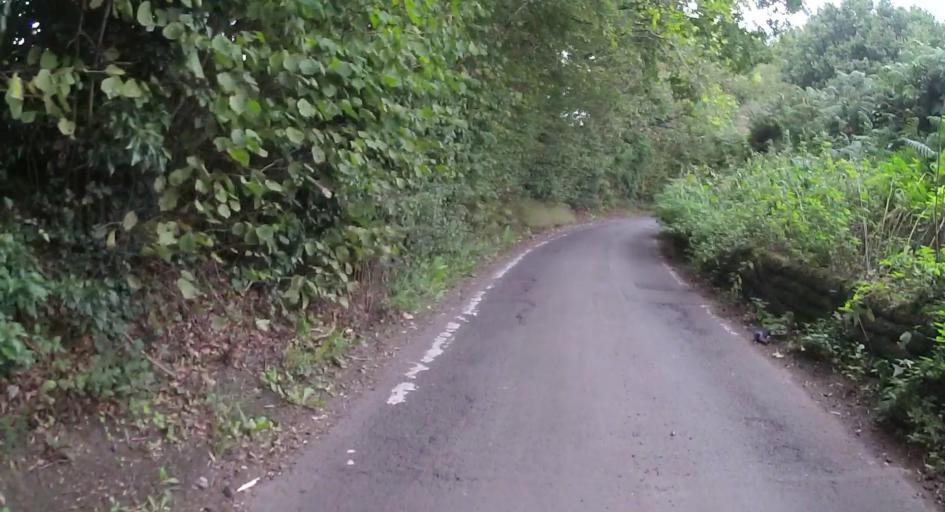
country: GB
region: England
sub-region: Surrey
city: Knaphill
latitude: 51.3256
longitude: -0.6211
